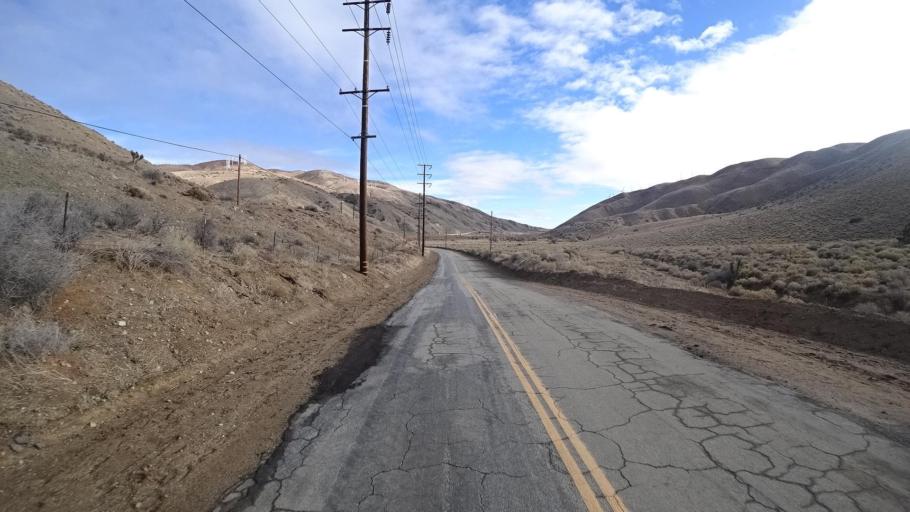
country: US
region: California
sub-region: Kern County
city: Mojave
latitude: 35.0926
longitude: -118.3073
